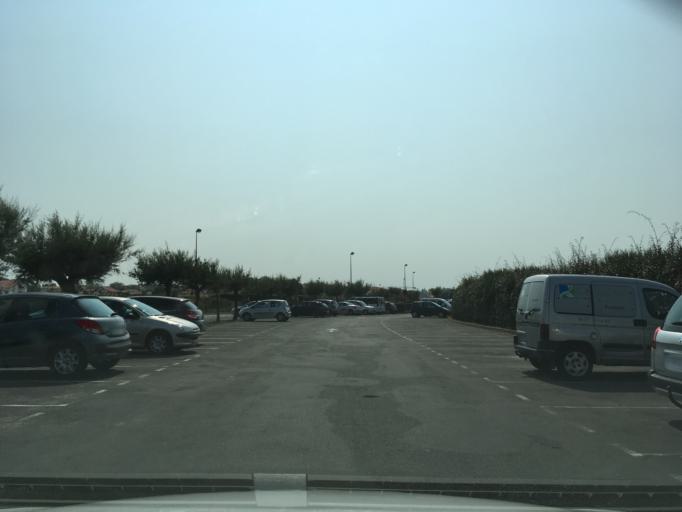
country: FR
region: Aquitaine
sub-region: Departement des Pyrenees-Atlantiques
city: Biarritz
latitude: 43.5052
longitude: -1.5365
